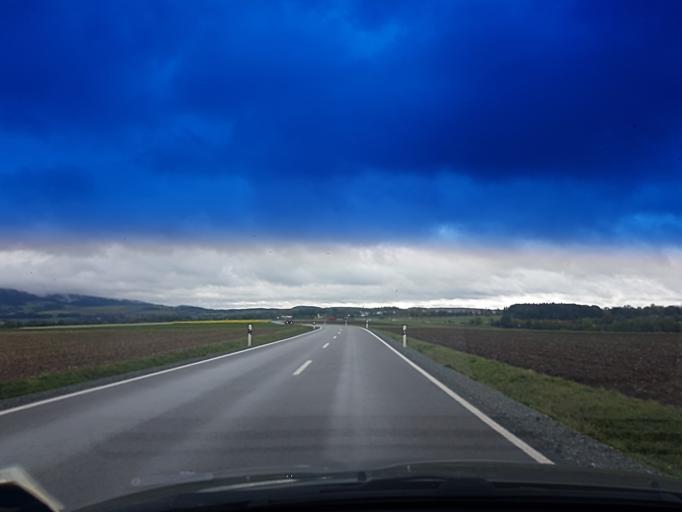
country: DE
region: Bavaria
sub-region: Upper Franconia
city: Bindlach
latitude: 50.0081
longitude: 11.6175
